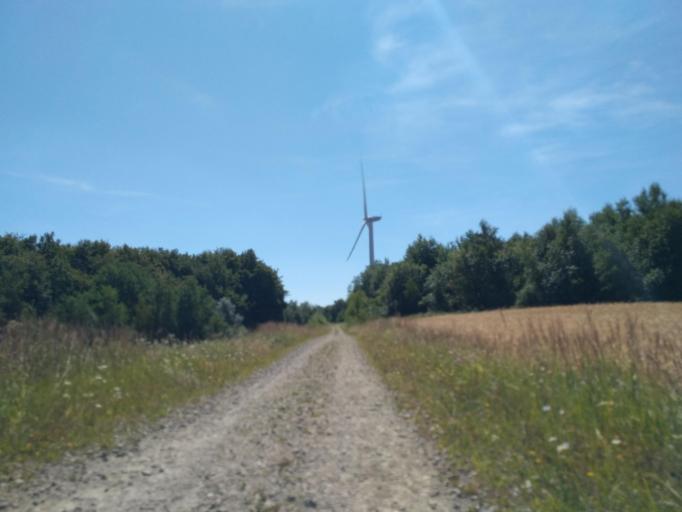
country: PL
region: Subcarpathian Voivodeship
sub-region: Powiat sanocki
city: Bukowsko
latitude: 49.5084
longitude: 22.0558
